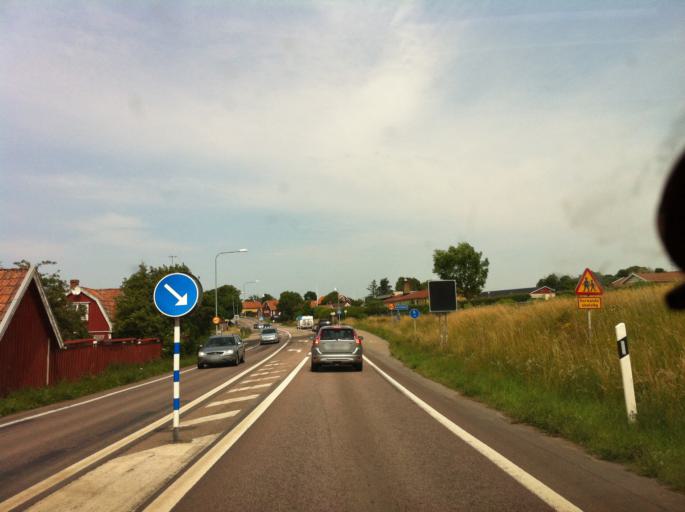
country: SE
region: Kalmar
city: Faerjestaden
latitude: 56.7165
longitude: 16.5346
